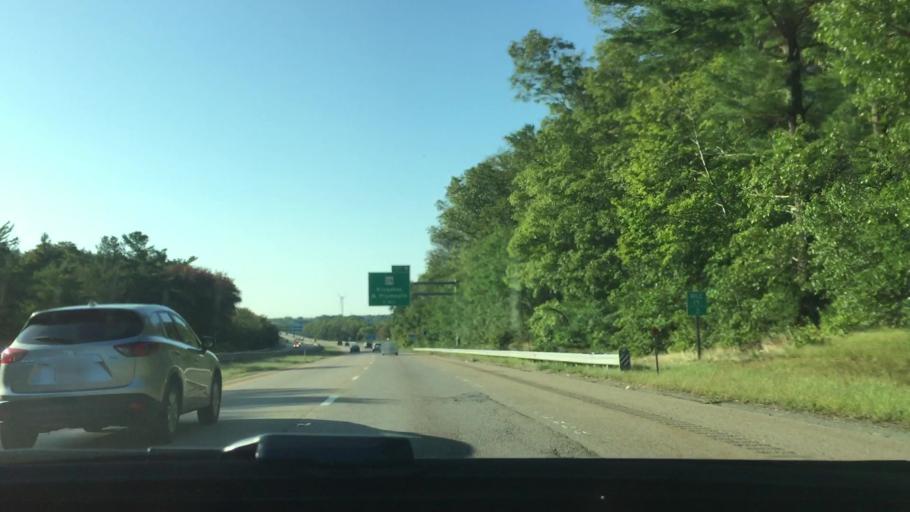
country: US
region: Massachusetts
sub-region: Plymouth County
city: Kingston
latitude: 42.0077
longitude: -70.7258
